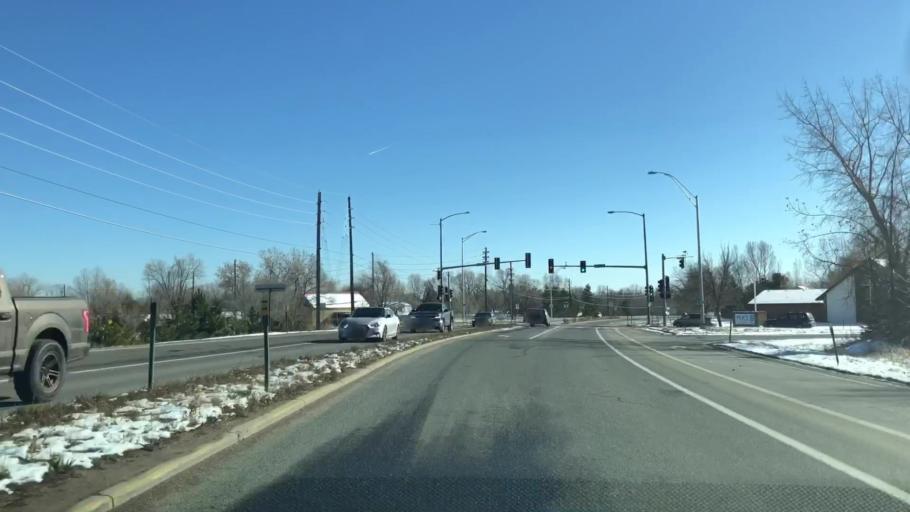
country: US
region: Colorado
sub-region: Boulder County
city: Boulder
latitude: 40.0517
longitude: -105.2607
